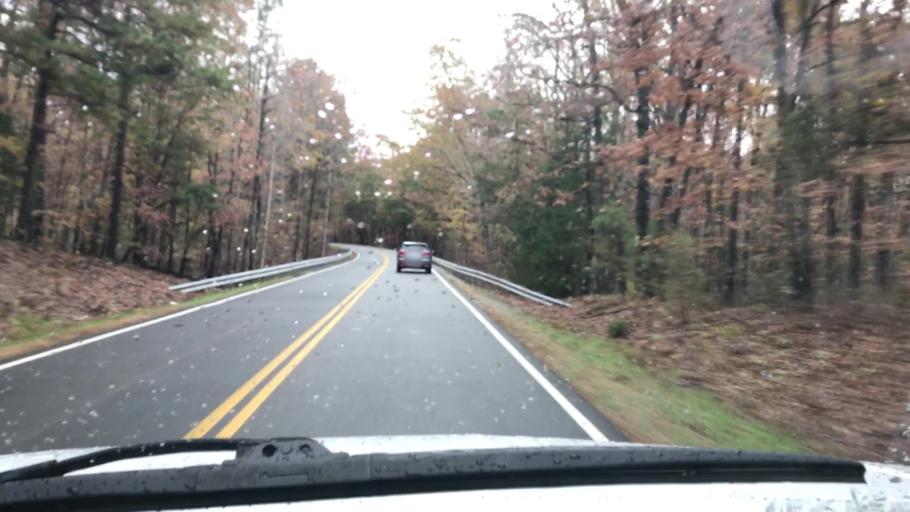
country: US
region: Virginia
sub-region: Henrico County
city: Short Pump
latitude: 37.6111
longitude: -77.6981
